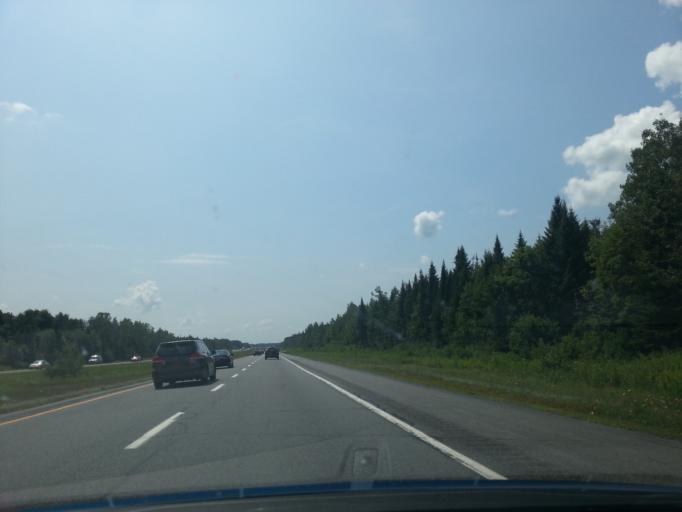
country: CA
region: Quebec
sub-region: Mauricie
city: Princeville
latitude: 46.3365
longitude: -71.9150
